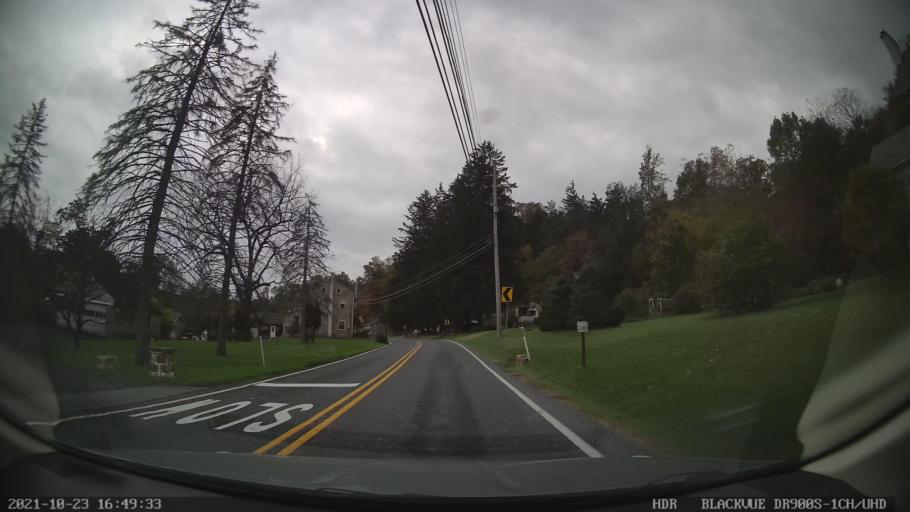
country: US
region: Pennsylvania
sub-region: Berks County
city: Red Lion
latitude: 40.4855
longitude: -75.6155
